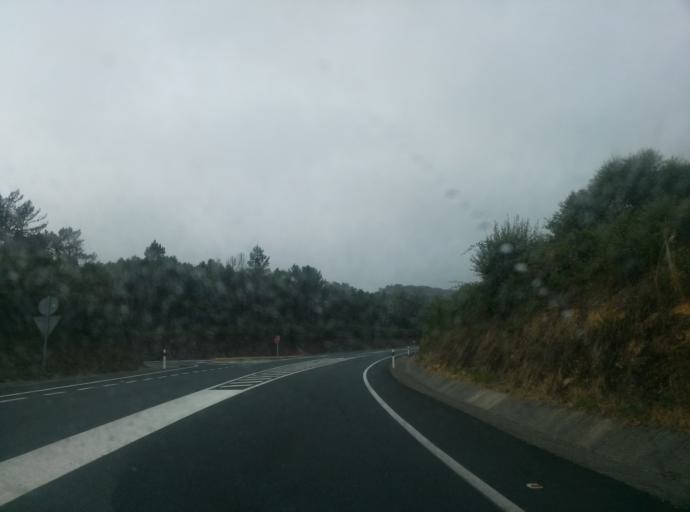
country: ES
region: Galicia
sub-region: Provincia de Lugo
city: Muras
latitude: 43.4281
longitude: -7.7570
